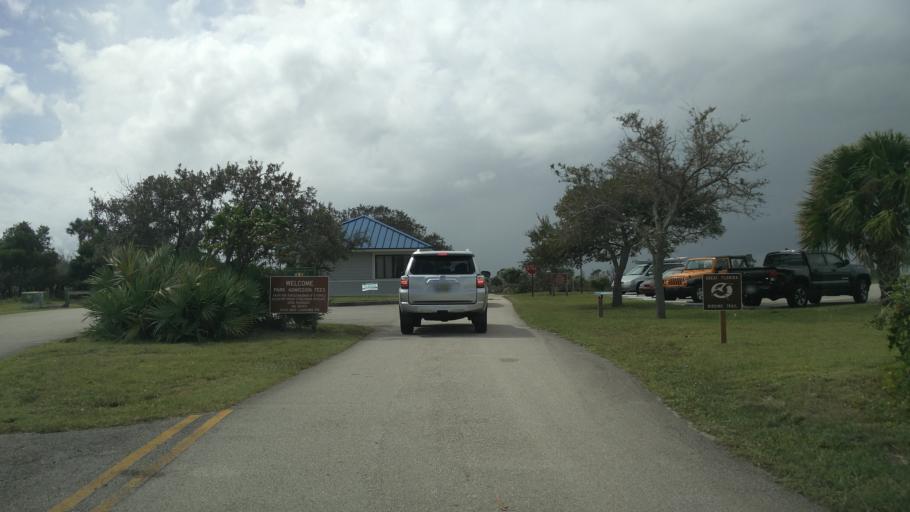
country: US
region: Florida
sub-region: Palm Beach County
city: Tequesta
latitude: 27.0035
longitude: -80.1009
